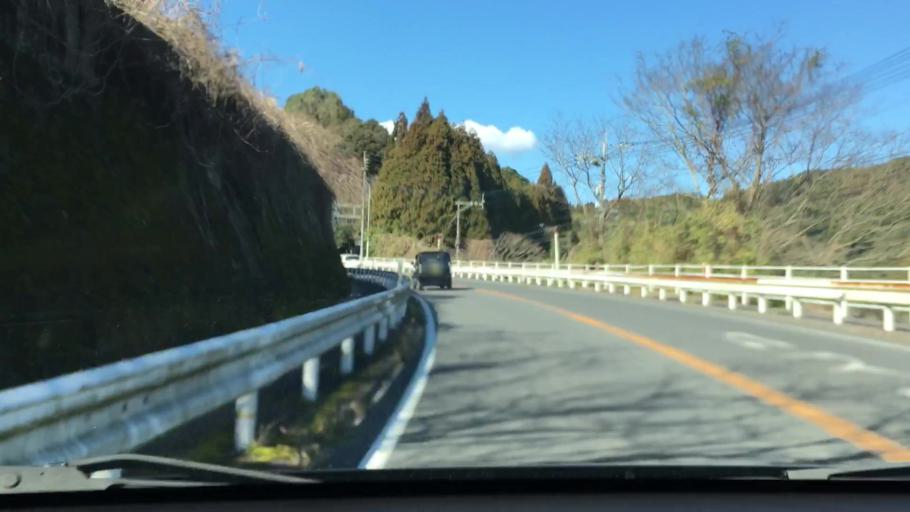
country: JP
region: Kagoshima
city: Ijuin
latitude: 31.6587
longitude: 130.4950
